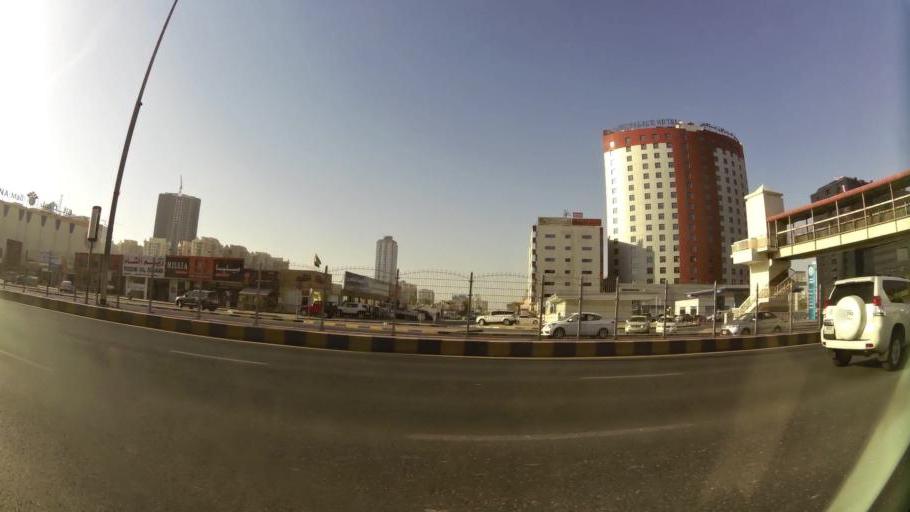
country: AE
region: Ajman
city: Ajman
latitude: 25.3889
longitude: 55.4603
